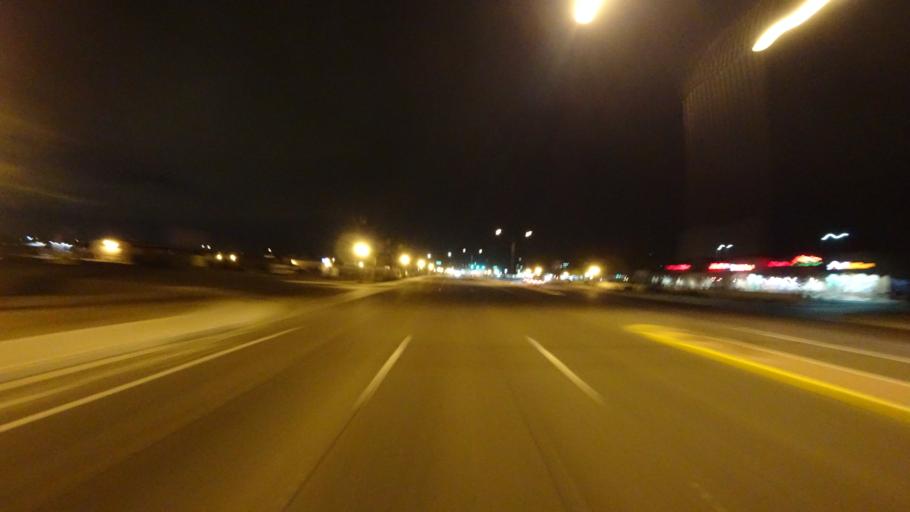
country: US
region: Arizona
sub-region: Maricopa County
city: Gilbert
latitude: 33.3051
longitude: -111.7212
